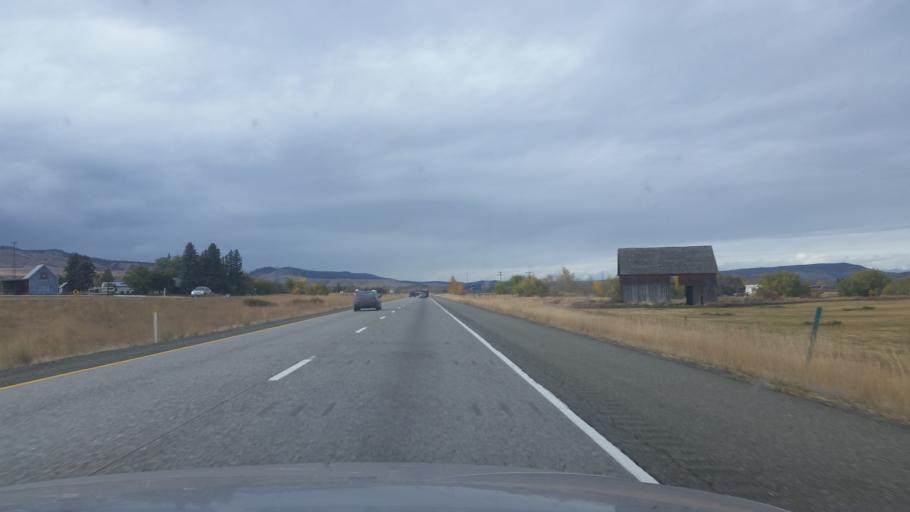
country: US
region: Washington
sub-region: Kittitas County
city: Ellensburg
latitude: 47.0638
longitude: -120.6935
